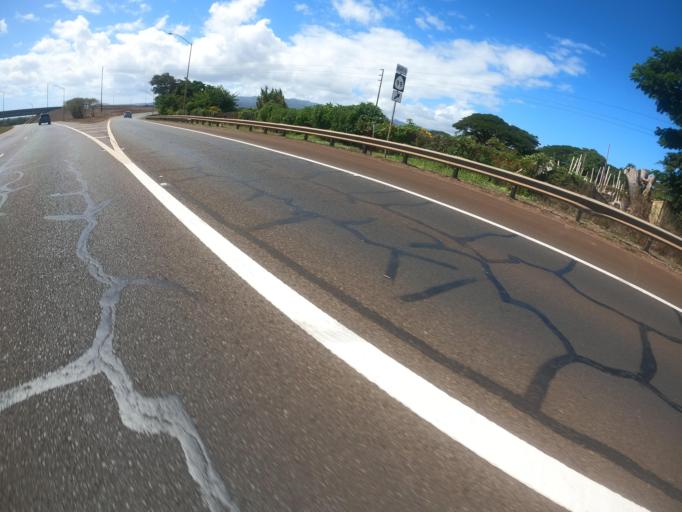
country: US
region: Hawaii
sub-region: Honolulu County
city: Pearl City, Manana
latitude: 21.3949
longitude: -157.9880
